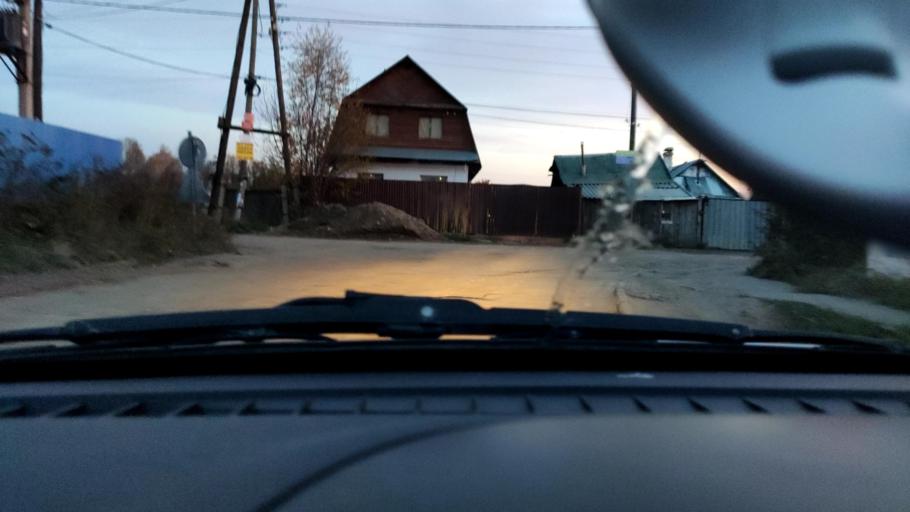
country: RU
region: Perm
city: Kondratovo
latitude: 58.0069
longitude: 56.0976
